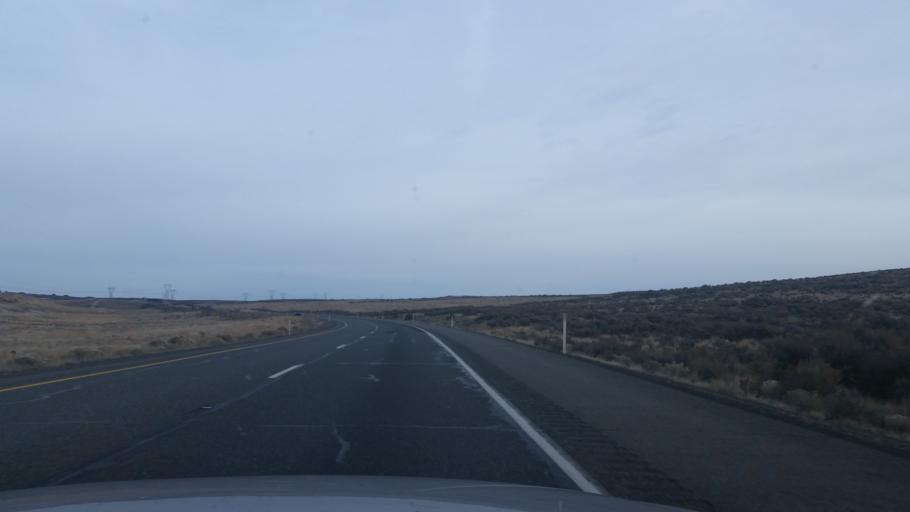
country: US
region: Washington
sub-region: Kittitas County
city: Kittitas
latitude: 46.9448
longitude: -120.2421
